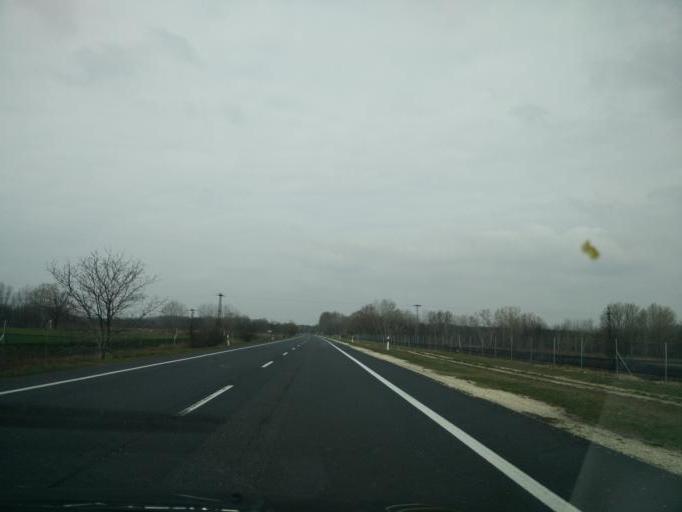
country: HU
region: Gyor-Moson-Sopron
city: Toltestava
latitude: 47.7053
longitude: 17.7591
